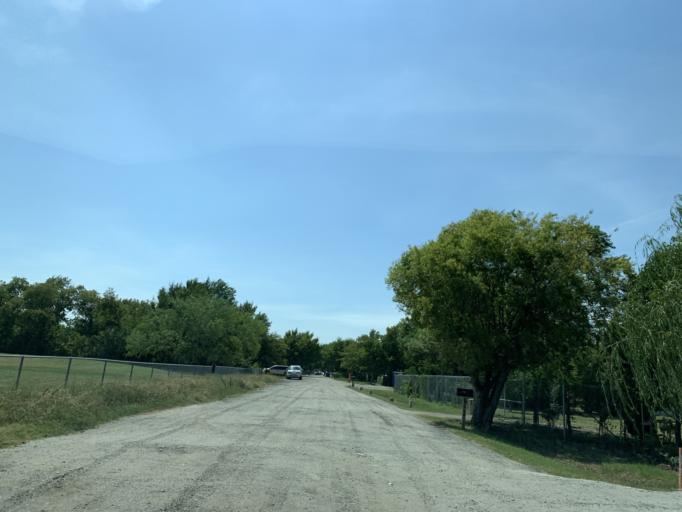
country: US
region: Texas
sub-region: Dallas County
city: Cedar Hill
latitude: 32.6522
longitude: -97.0129
